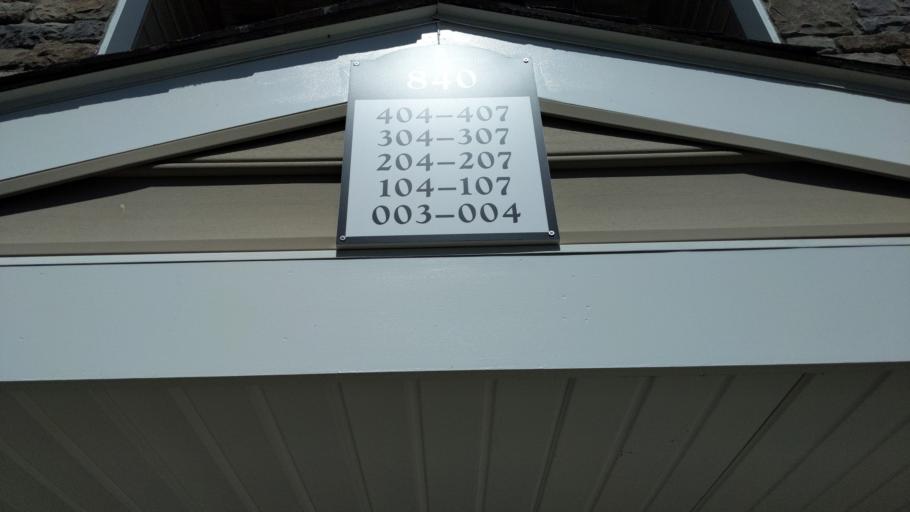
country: US
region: Virginia
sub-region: Montgomery County
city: Blacksburg
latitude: 37.2234
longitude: -80.4422
